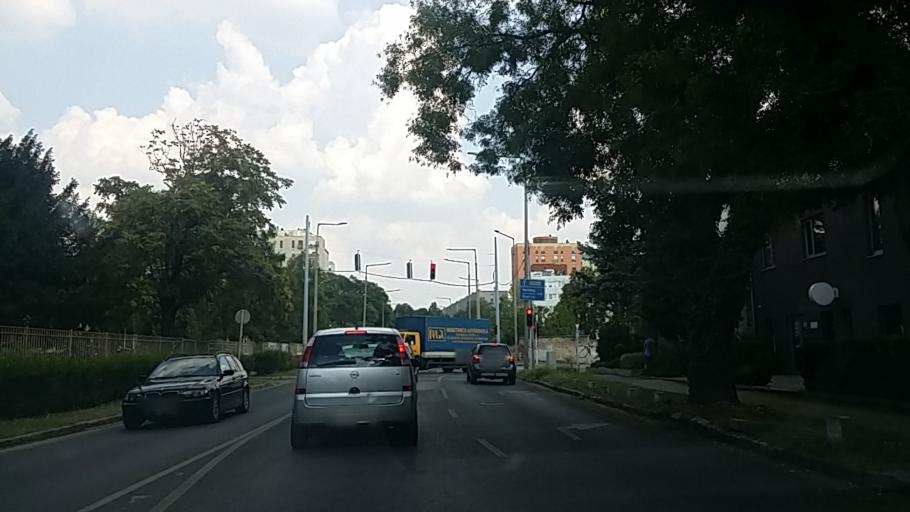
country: HU
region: Baranya
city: Pecs
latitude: 46.0722
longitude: 18.2055
